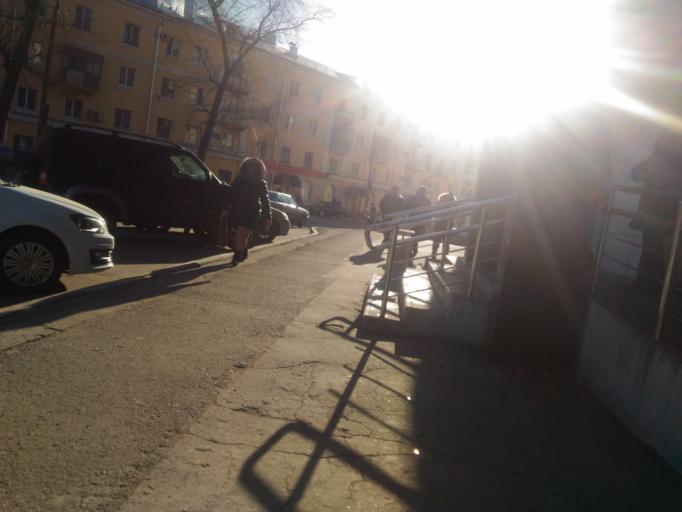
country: RU
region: Ulyanovsk
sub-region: Ulyanovskiy Rayon
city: Ulyanovsk
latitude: 54.3232
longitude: 48.3887
